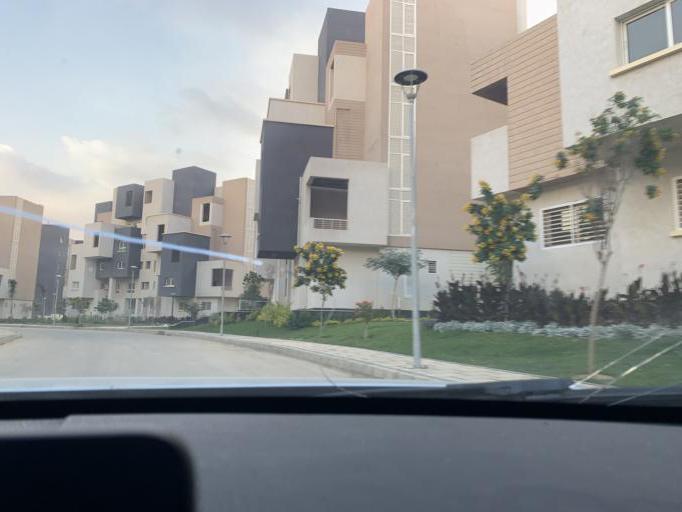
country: EG
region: Muhafazat al Qalyubiyah
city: Al Khankah
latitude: 30.0990
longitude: 31.6532
